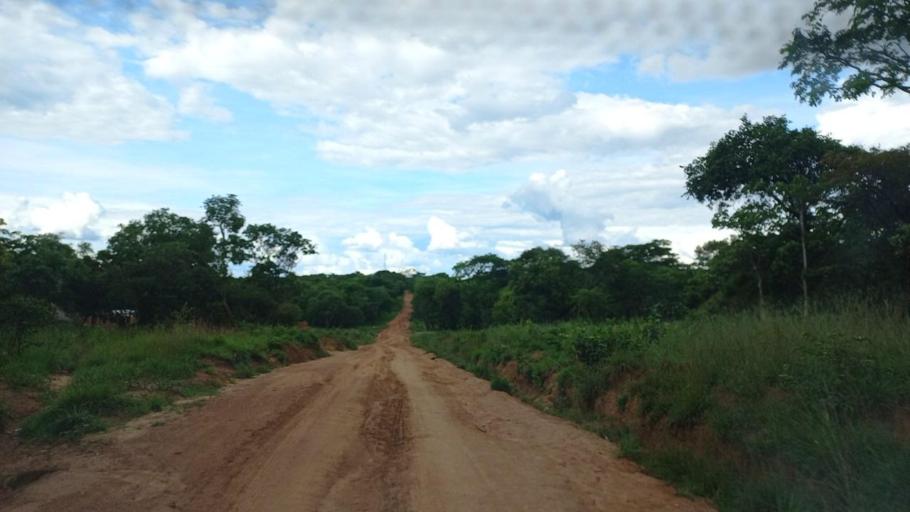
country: ZM
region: North-Western
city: Mwinilunga
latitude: -11.8390
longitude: 24.3657
